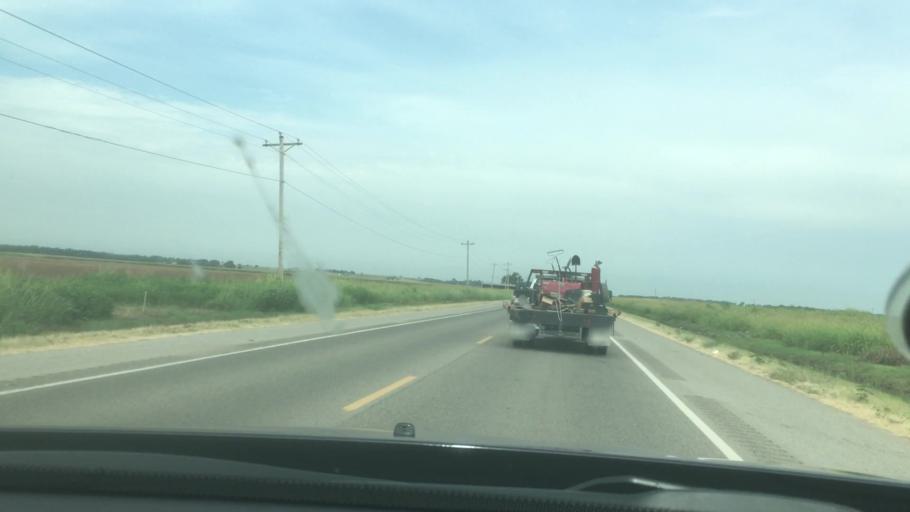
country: US
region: Oklahoma
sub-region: Garvin County
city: Lindsay
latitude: 34.8234
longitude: -97.5299
